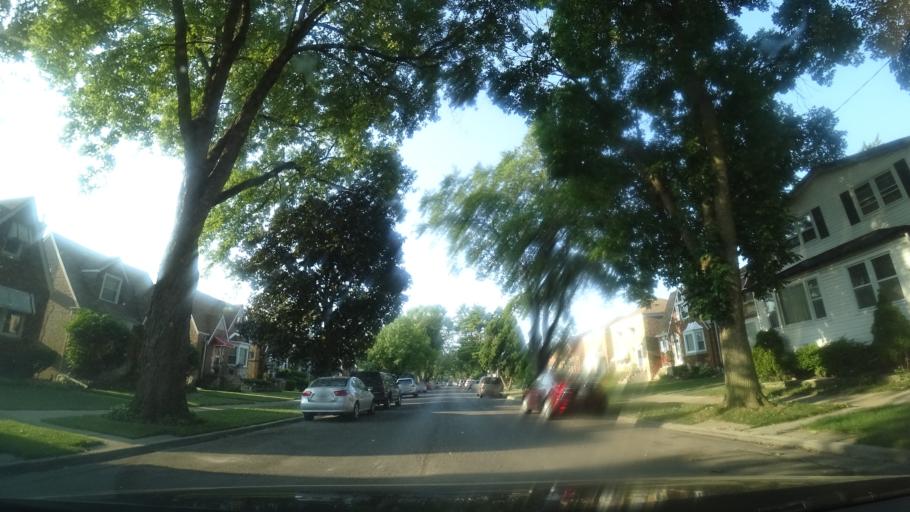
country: US
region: Illinois
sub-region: Cook County
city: Elmwood Park
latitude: 41.9341
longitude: -87.7785
